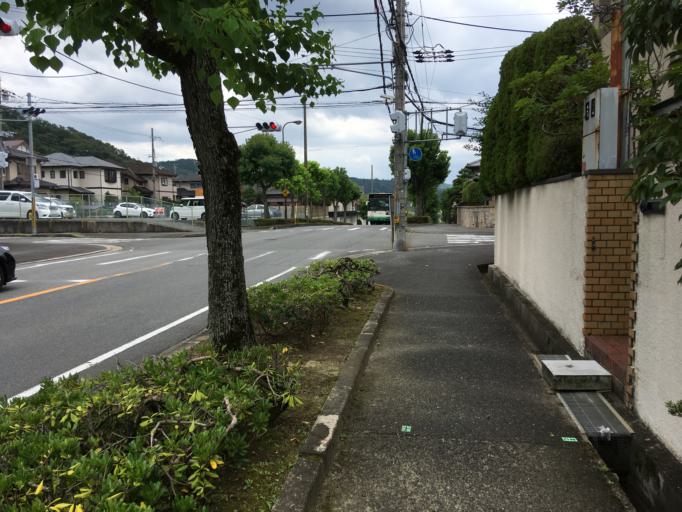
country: JP
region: Nara
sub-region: Ikoma-shi
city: Ikoma
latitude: 34.6780
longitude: 135.7188
